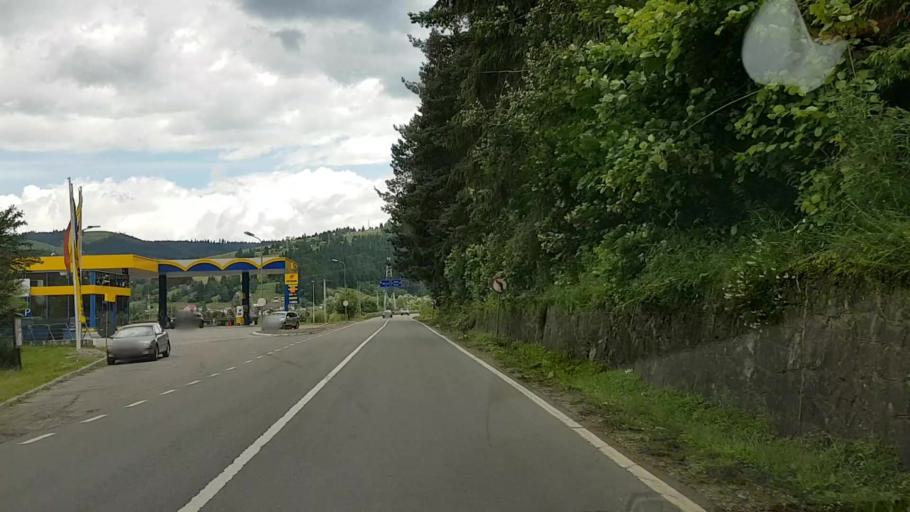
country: RO
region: Neamt
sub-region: Comuna Poiana Teiului
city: Poiana Teiului
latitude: 47.0919
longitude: 25.9554
